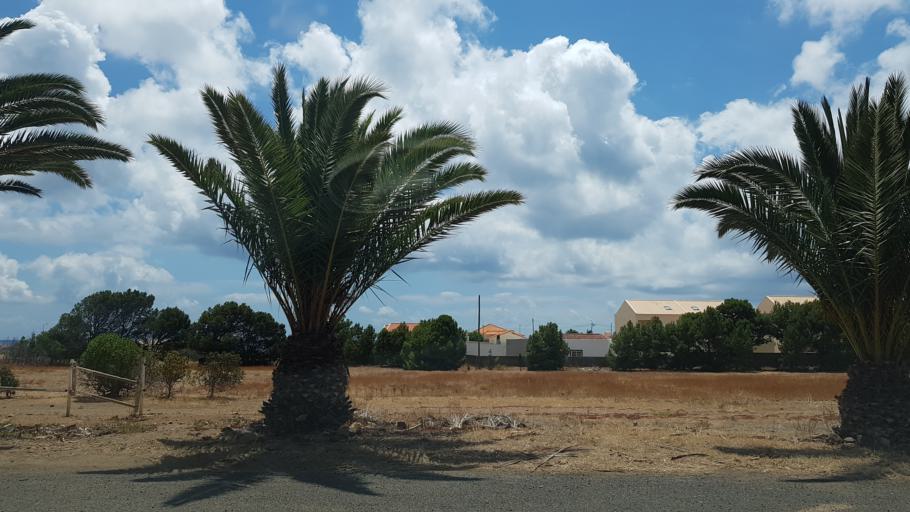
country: PT
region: Madeira
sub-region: Porto Santo
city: Vila de Porto Santo
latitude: 33.0367
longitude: -16.3721
